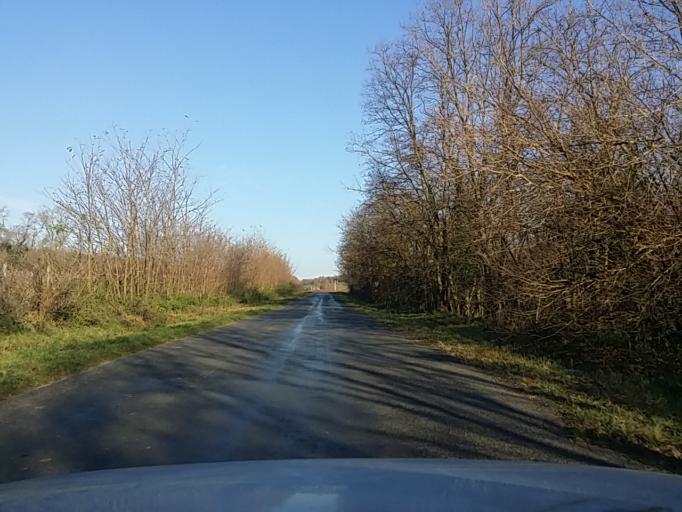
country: HU
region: Veszprem
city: Badacsonytomaj
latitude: 46.8241
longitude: 17.5145
